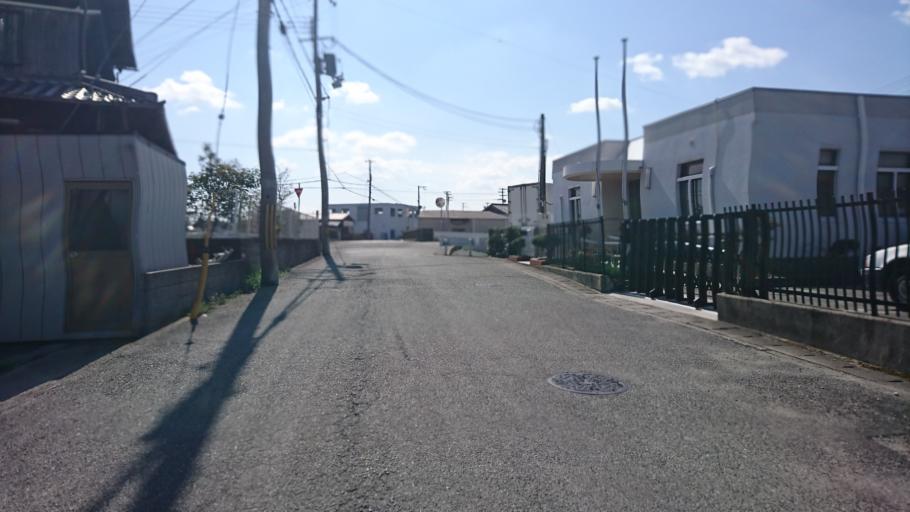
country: JP
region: Hyogo
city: Kakogawacho-honmachi
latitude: 34.8097
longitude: 134.8191
